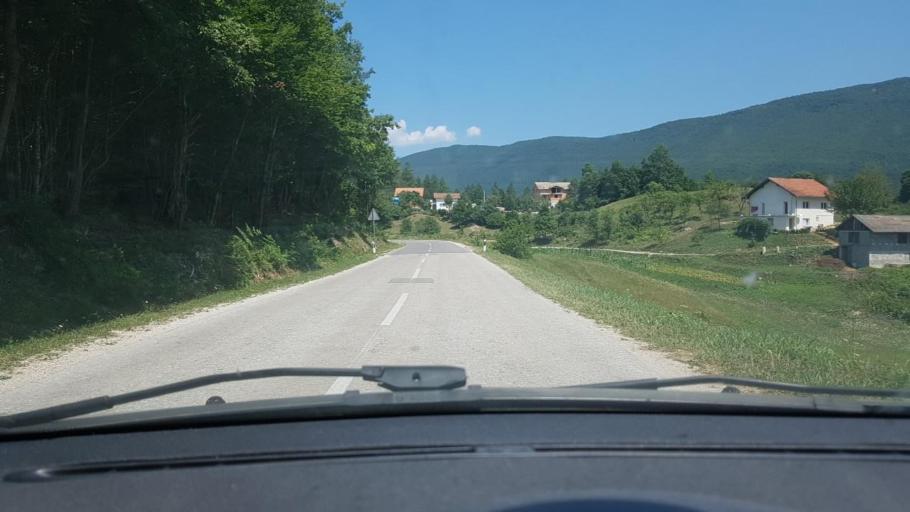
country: BA
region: Federation of Bosnia and Herzegovina
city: Orasac
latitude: 44.6099
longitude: 16.0711
